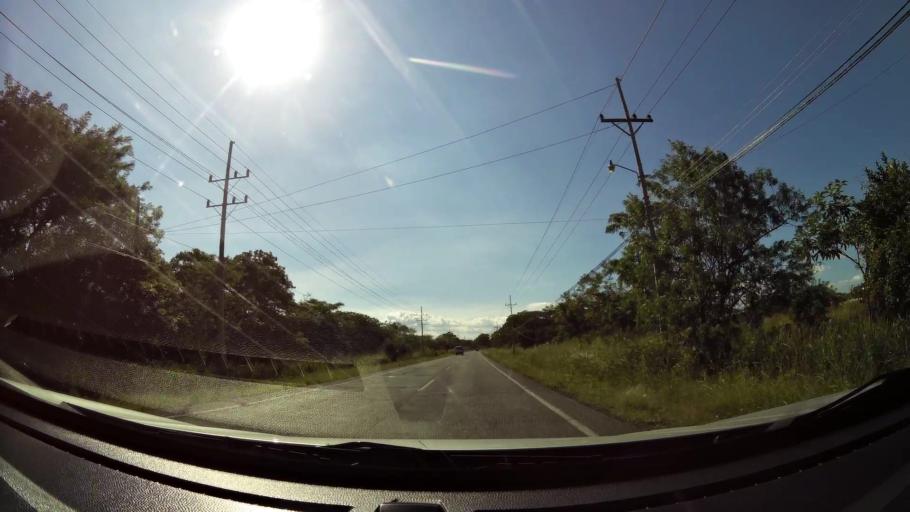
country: CR
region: Guanacaste
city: Liberia
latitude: 10.6156
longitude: -85.4735
